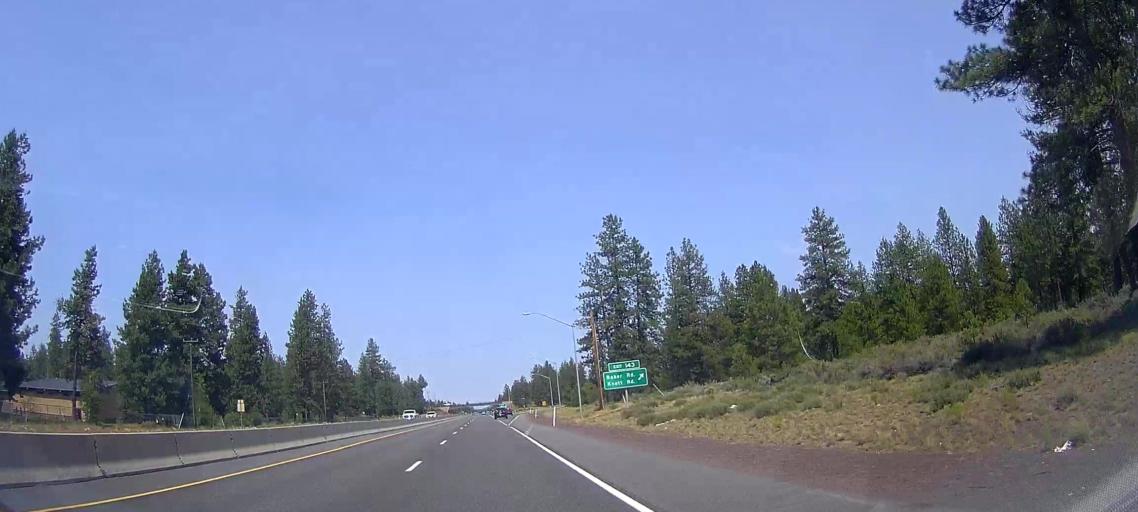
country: US
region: Oregon
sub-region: Deschutes County
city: Deschutes River Woods
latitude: 43.9884
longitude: -121.3376
